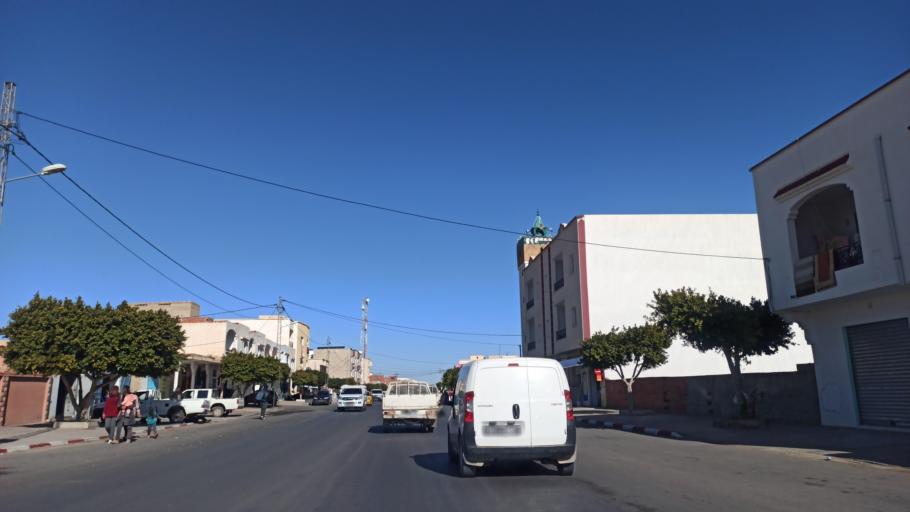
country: TN
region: Sidi Bu Zayd
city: Bi'r al Hufayy
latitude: 34.9251
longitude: 9.1905
